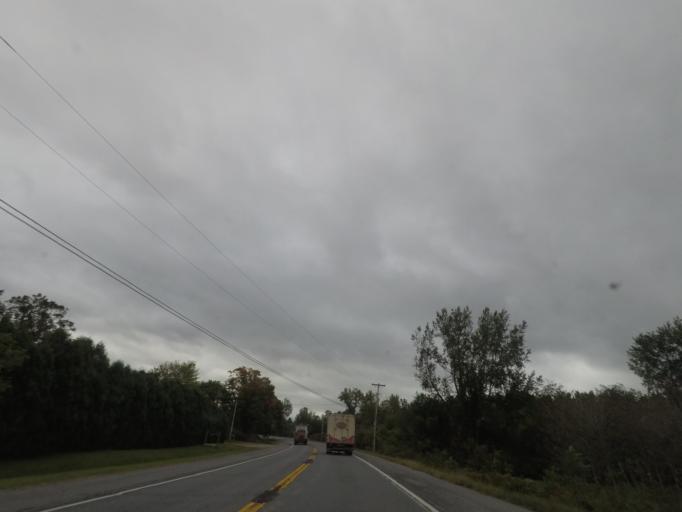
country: US
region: New York
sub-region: Rensselaer County
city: Hoosick Falls
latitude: 42.9349
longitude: -73.3636
